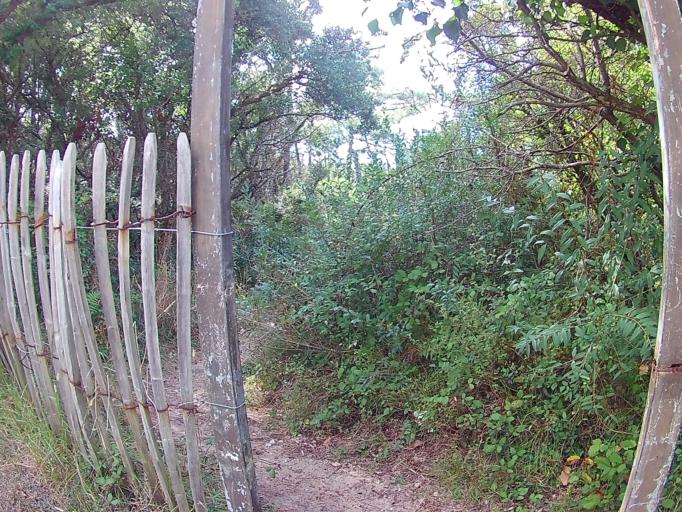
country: FR
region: Aquitaine
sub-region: Departement des Landes
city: Labenne
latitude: 43.6010
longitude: -1.4683
